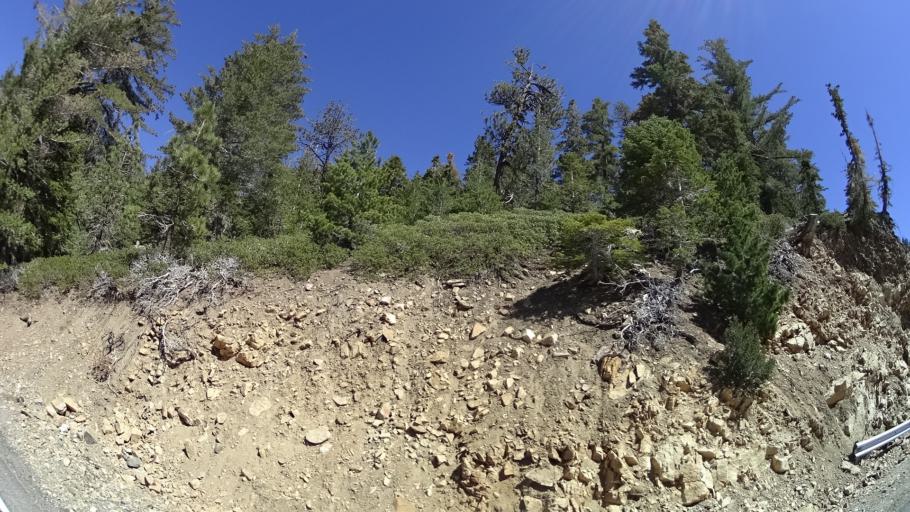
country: US
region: California
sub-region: San Bernardino County
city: Pinon Hills
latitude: 34.3729
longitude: -117.7818
